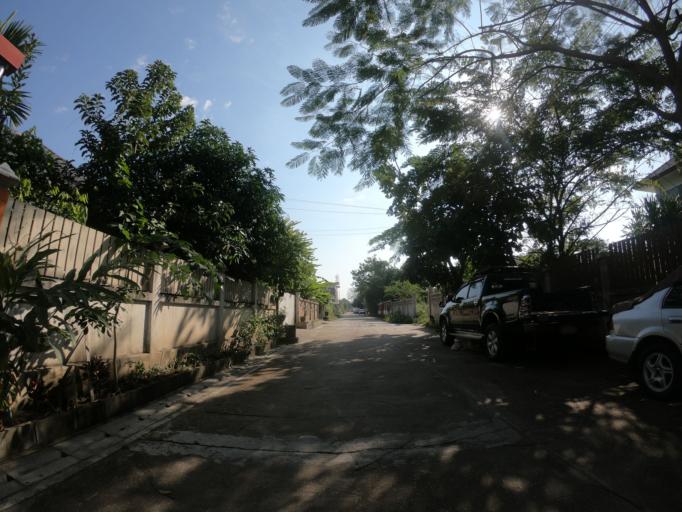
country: TH
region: Chiang Mai
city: Chiang Mai
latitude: 18.7512
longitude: 98.9839
